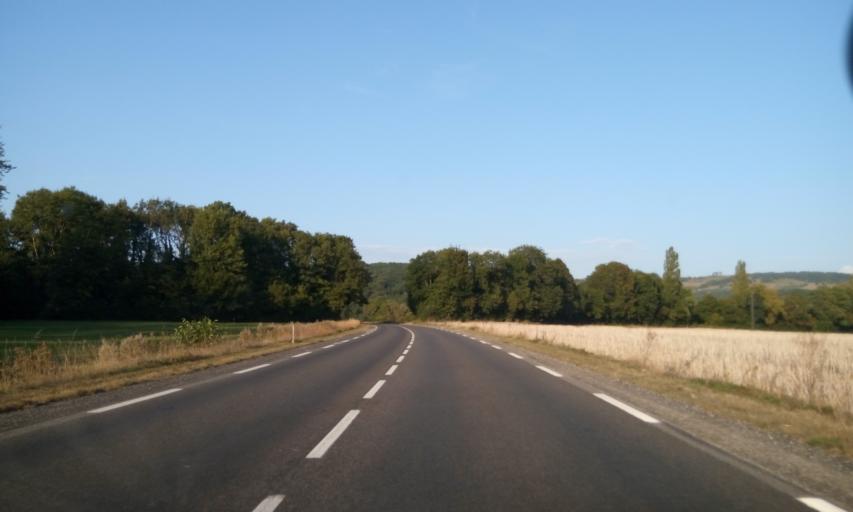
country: FR
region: Rhone-Alpes
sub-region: Departement de l'Ain
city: Saint-Jean-le-Vieux
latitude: 46.0458
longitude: 5.3780
